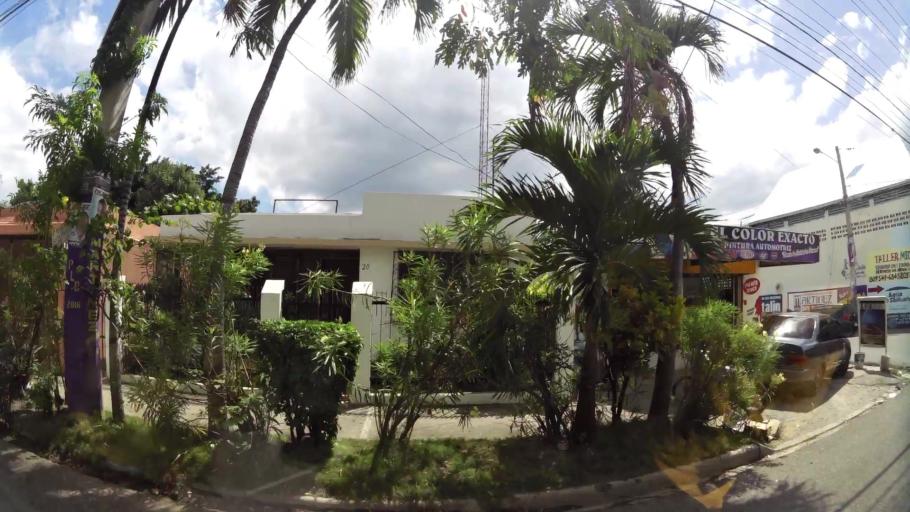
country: DO
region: San Cristobal
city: San Cristobal
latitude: 18.4137
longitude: -70.1157
